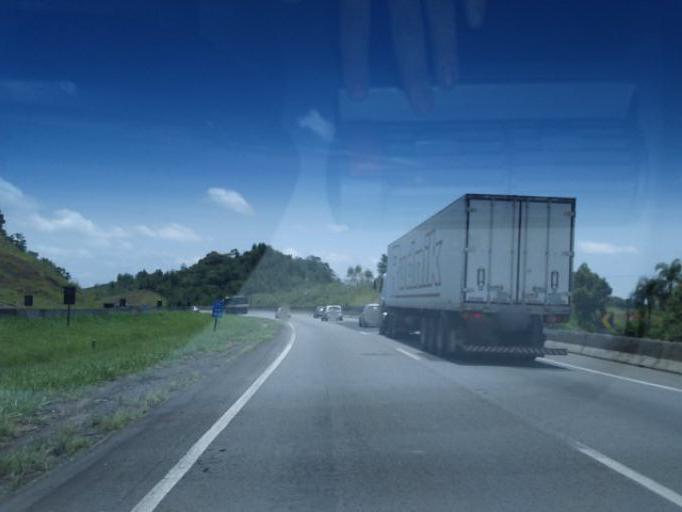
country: BR
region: Sao Paulo
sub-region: Juquia
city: Juquia
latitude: -24.3323
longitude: -47.6386
